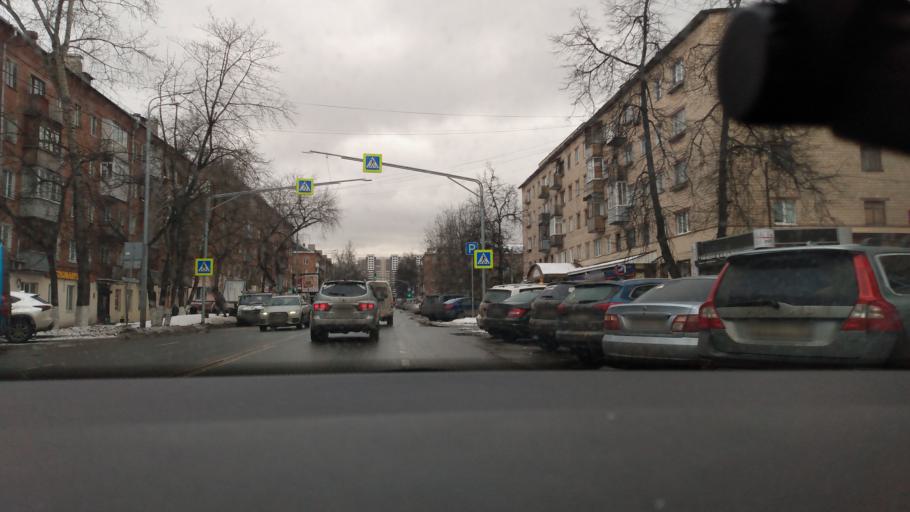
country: RU
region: Moskovskaya
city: Balashikha
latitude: 55.8015
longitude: 37.9348
